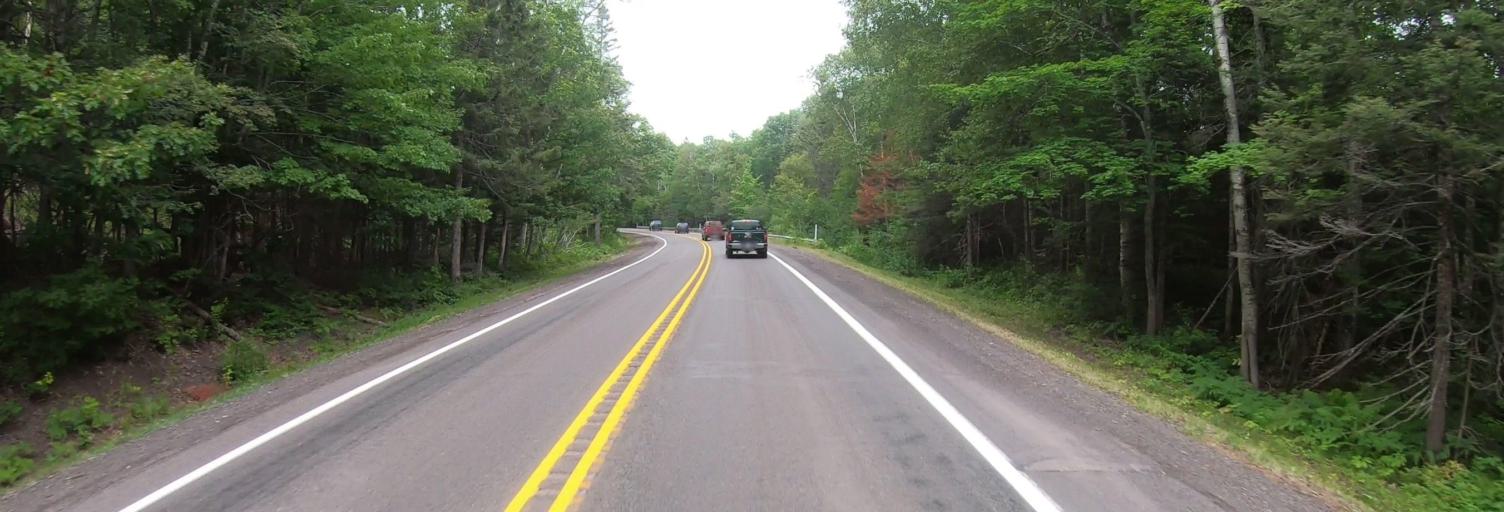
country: US
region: Michigan
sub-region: Keweenaw County
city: Eagle River
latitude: 47.3988
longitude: -88.2482
